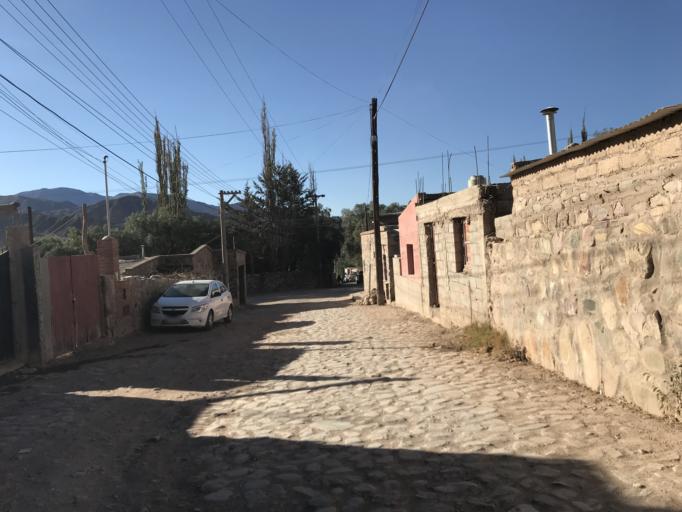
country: AR
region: Jujuy
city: Maimara
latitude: -23.5801
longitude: -65.3962
